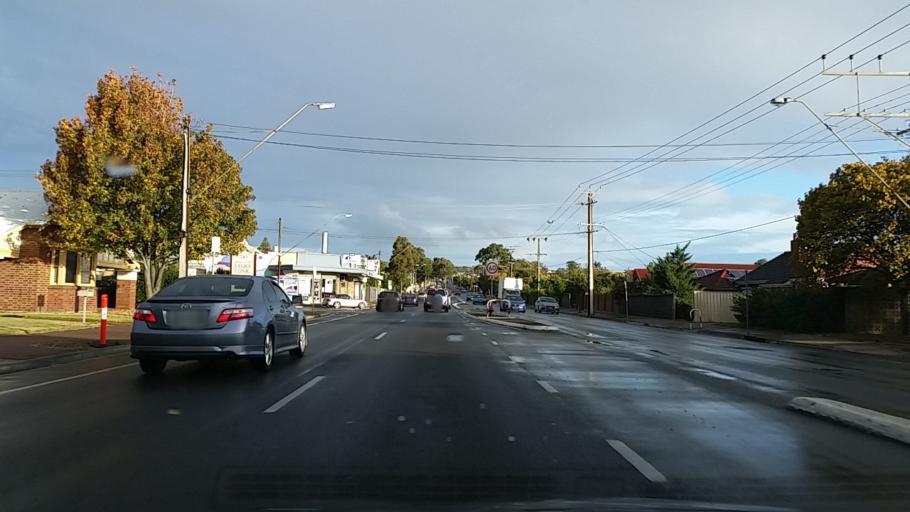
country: AU
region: South Australia
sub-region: Adelaide
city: Brighton
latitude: -35.0237
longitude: 138.5235
